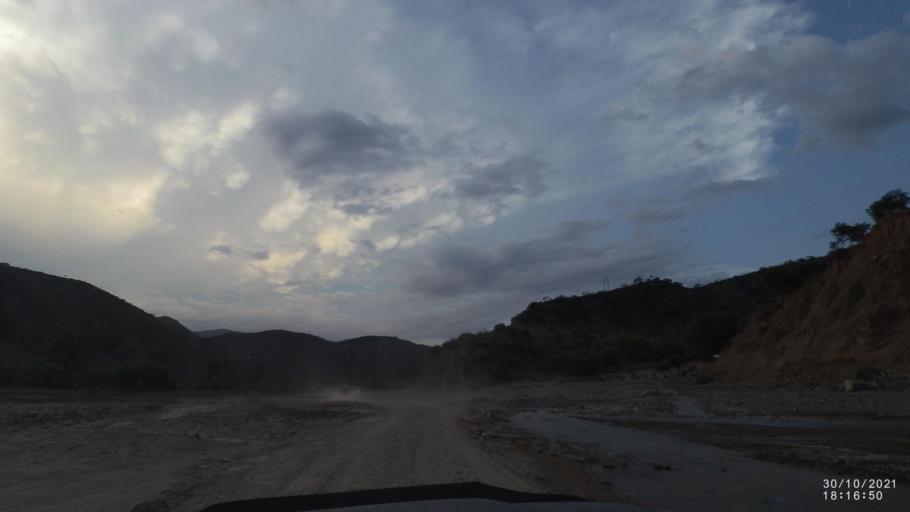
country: BO
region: Cochabamba
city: Sipe Sipe
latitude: -17.5447
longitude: -66.4280
